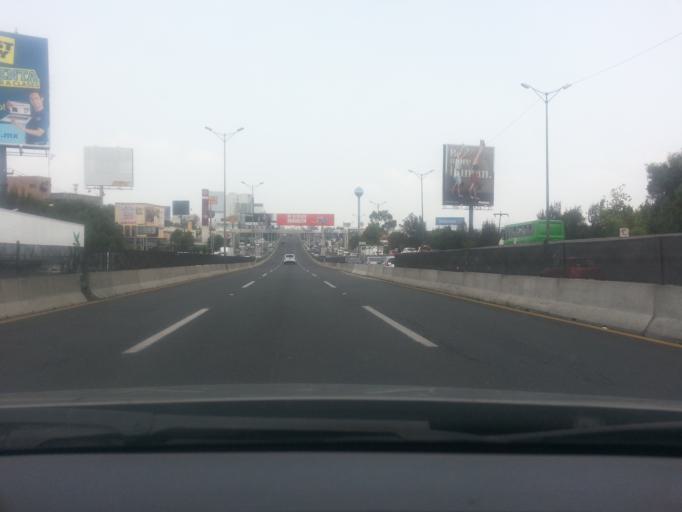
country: MX
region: Mexico
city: Vista Hermosa
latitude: 19.5138
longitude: -99.2345
